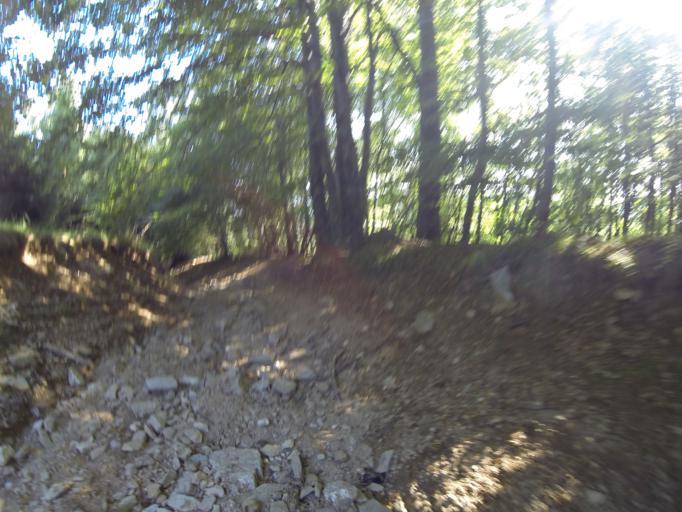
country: RO
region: Valcea
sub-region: Comuna Vaideeni
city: Vaideeni
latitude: 45.2350
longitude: 23.9600
